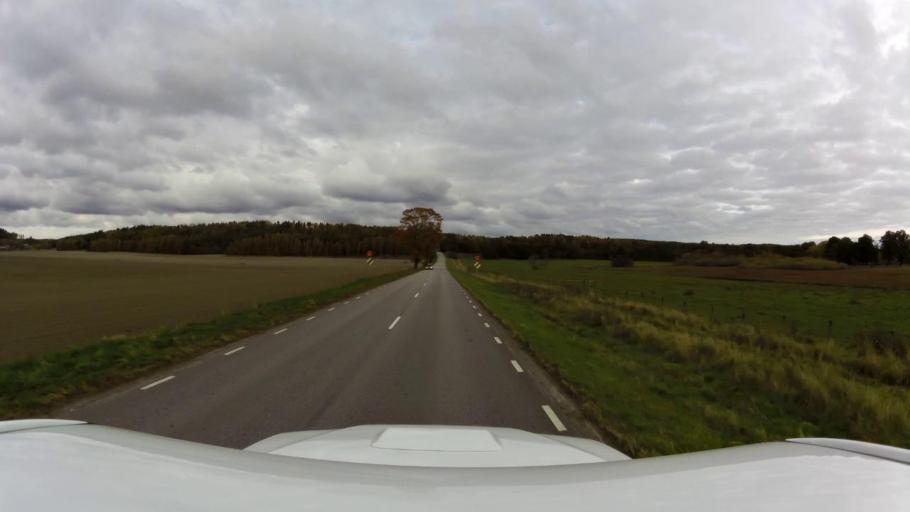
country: SE
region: OEstergoetland
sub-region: Linkopings Kommun
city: Berg
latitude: 58.5031
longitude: 15.5387
